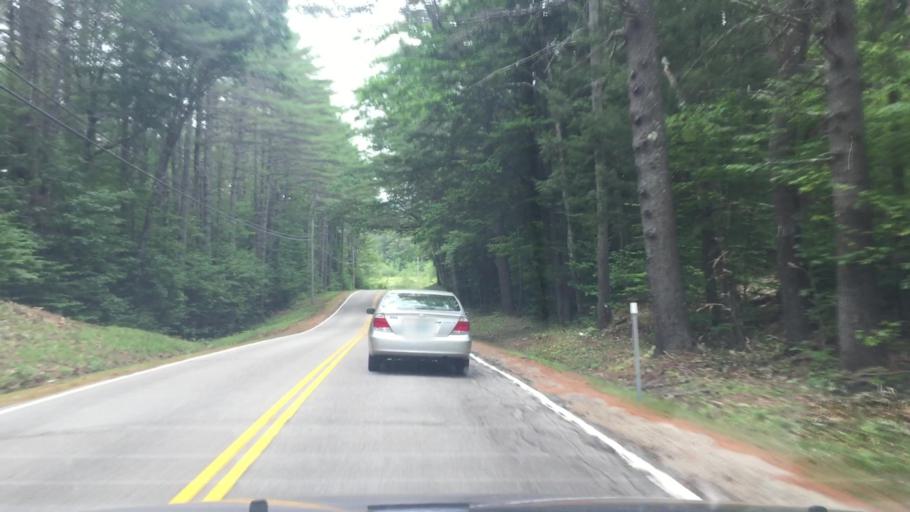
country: US
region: New Hampshire
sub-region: Carroll County
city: Conway
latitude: 43.9243
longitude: -71.0779
